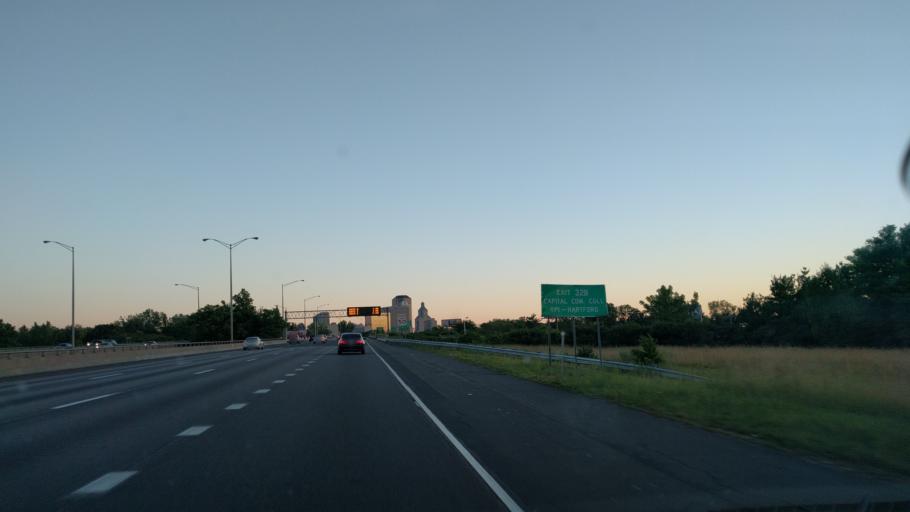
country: US
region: Connecticut
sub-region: Hartford County
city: Hartford
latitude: 41.7842
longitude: -72.6606
